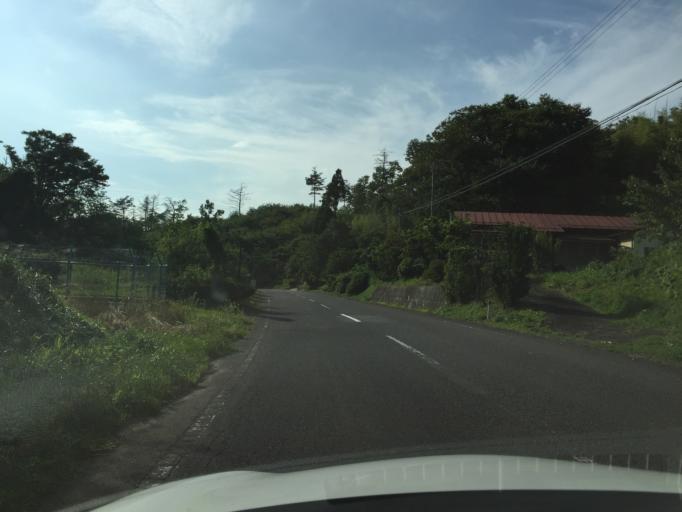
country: JP
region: Fukushima
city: Miharu
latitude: 37.3672
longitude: 140.5165
